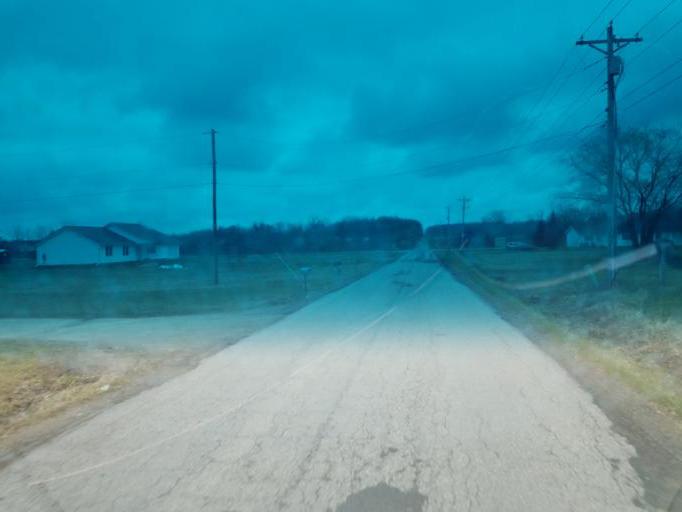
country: US
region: Ohio
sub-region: Morrow County
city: Mount Gilead
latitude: 40.4598
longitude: -82.7834
